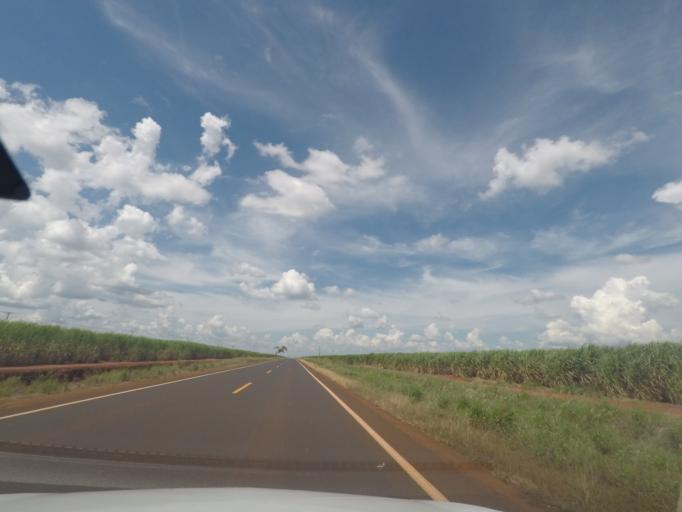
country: BR
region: Minas Gerais
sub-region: Conceicao Das Alagoas
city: Conceicao das Alagoas
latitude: -19.8658
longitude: -48.6108
